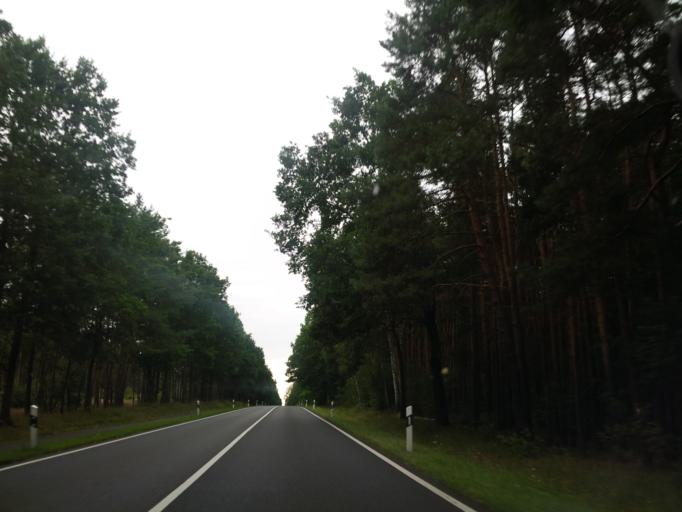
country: DE
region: Brandenburg
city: Treuenbrietzen
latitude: 52.0459
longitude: 12.9179
